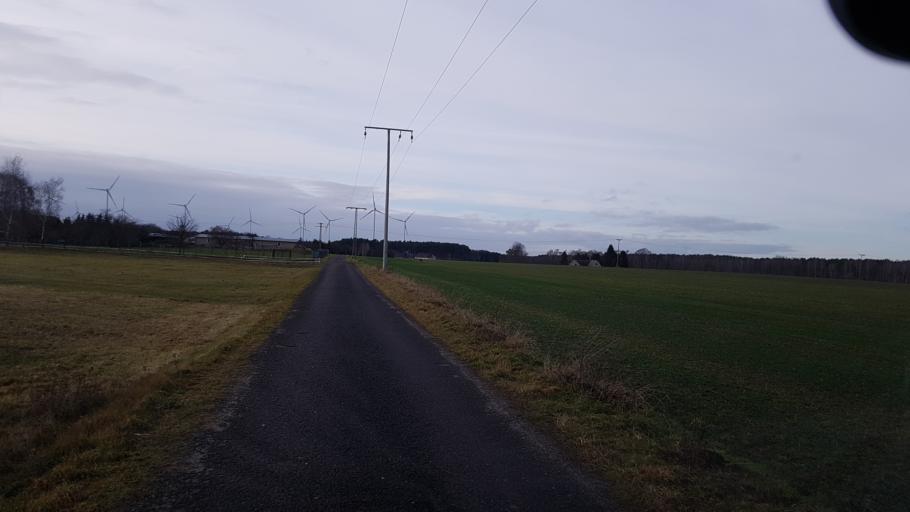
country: DE
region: Brandenburg
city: Sallgast
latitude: 51.6418
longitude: 13.8594
